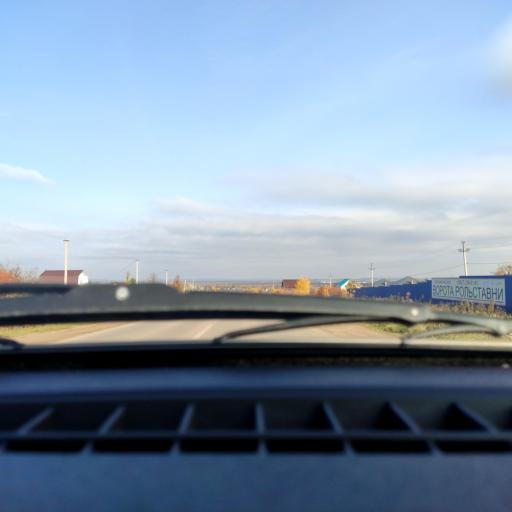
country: RU
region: Bashkortostan
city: Kabakovo
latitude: 54.7120
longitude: 56.1697
